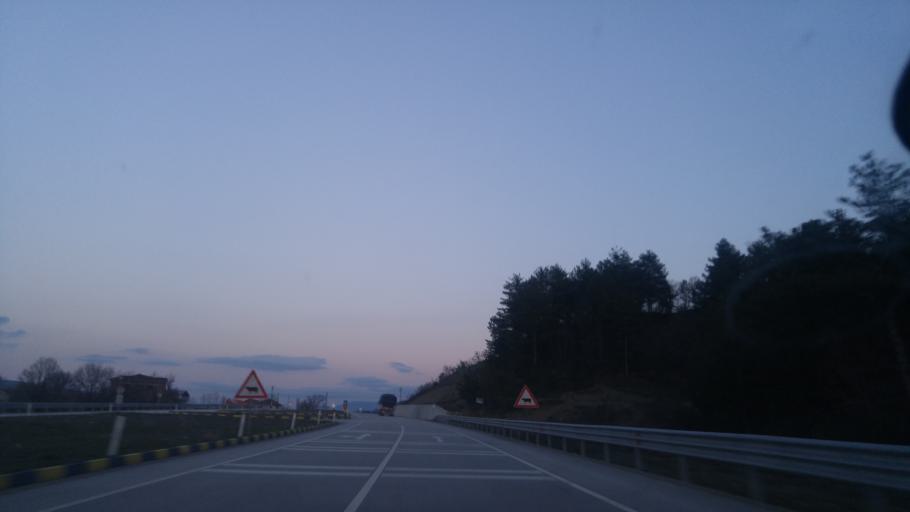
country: TR
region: Kastamonu
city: Igdir
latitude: 41.2301
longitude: 33.0816
